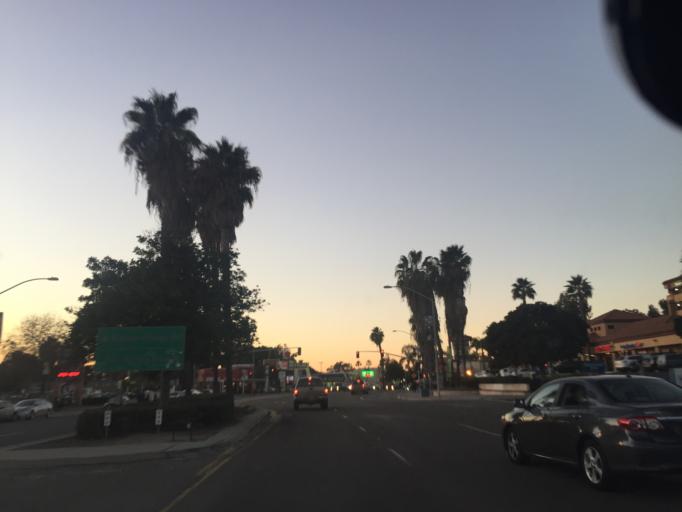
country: MX
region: Baja California
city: Tijuana
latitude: 32.5470
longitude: -117.0330
